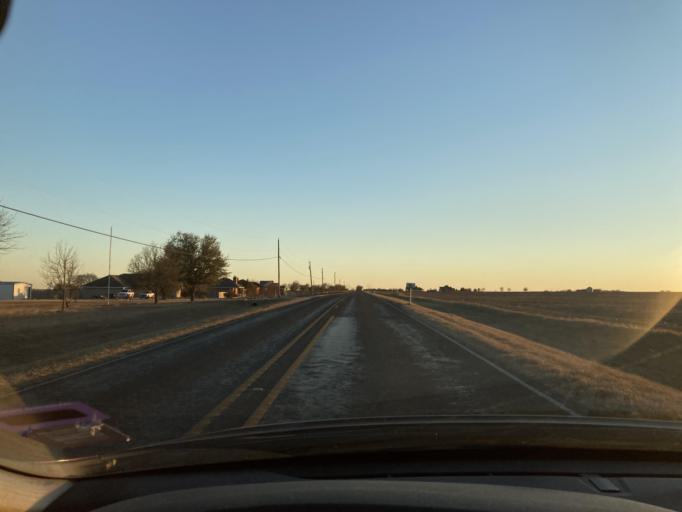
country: US
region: Texas
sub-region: Ellis County
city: Waxahachie
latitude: 32.3365
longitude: -96.8740
